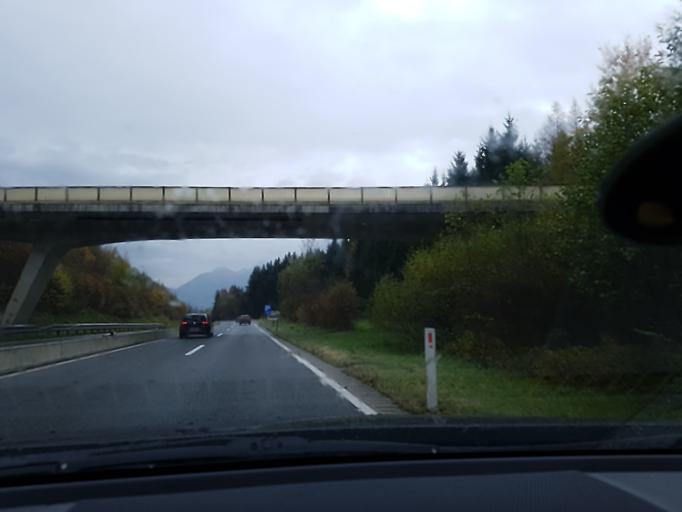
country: AT
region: Salzburg
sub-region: Politischer Bezirk Sankt Johann im Pongau
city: Bischofshofen
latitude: 47.4313
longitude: 13.2247
